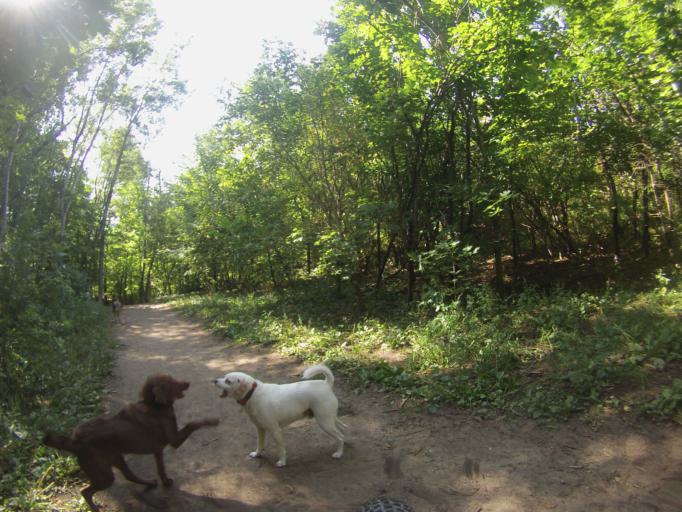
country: CA
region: Ontario
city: Ottawa
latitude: 45.3597
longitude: -75.6190
